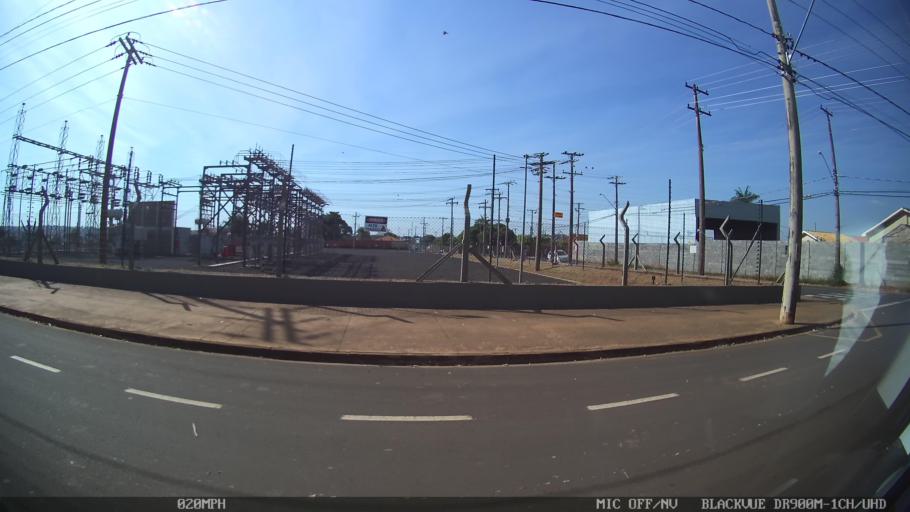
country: BR
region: Sao Paulo
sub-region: Sao Jose Do Rio Preto
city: Sao Jose do Rio Preto
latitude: -20.7889
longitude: -49.3804
